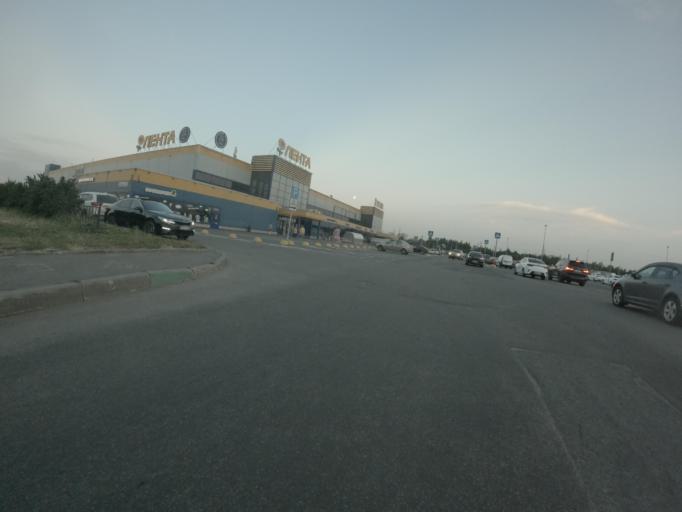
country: RU
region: St.-Petersburg
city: Krasnogvargeisky
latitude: 59.9352
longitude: 30.4966
